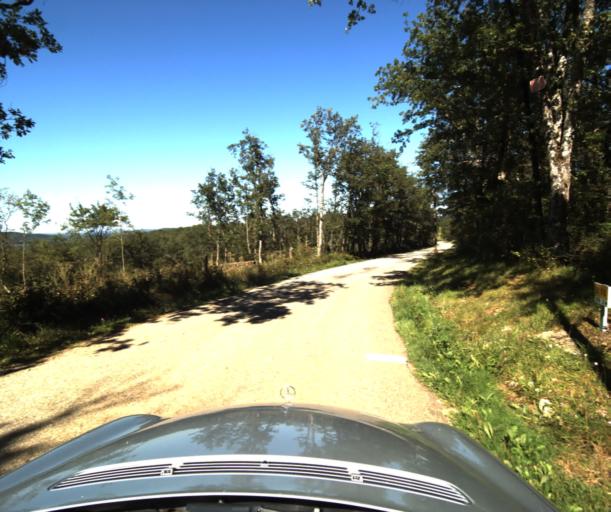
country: FR
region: Midi-Pyrenees
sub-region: Departement de l'Ariege
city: Lavelanet
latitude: 42.9641
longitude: 1.9033
